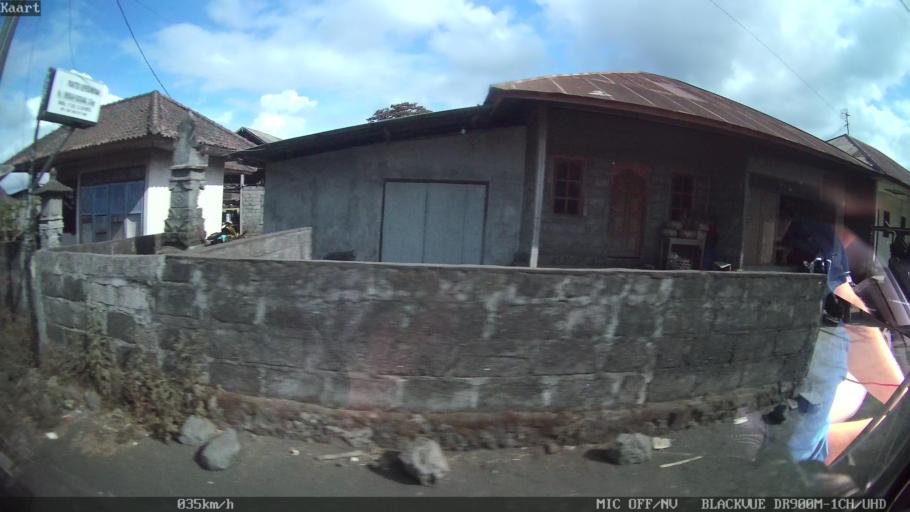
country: ID
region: Bali
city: Banjar Trunyan
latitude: -8.2163
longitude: 115.3838
